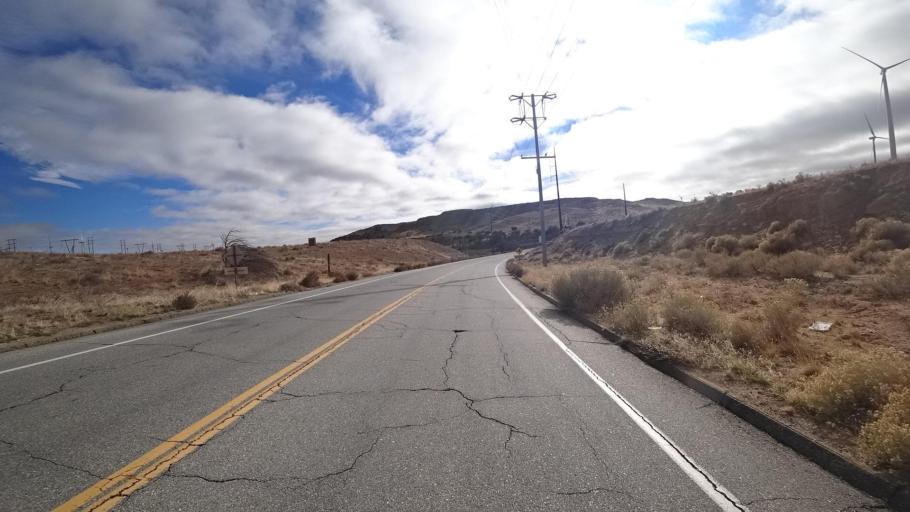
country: US
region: California
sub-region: Kern County
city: Tehachapi
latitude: 35.0517
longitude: -118.3570
